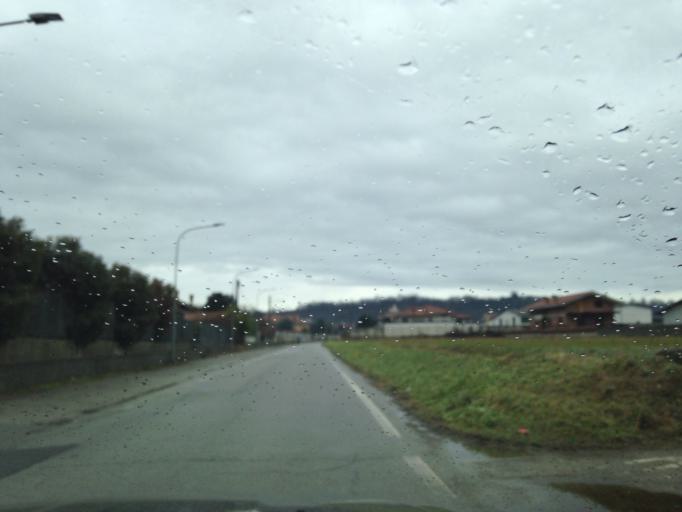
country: IT
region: Piedmont
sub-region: Provincia di Torino
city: Villareggia
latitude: 45.3053
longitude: 7.9779
